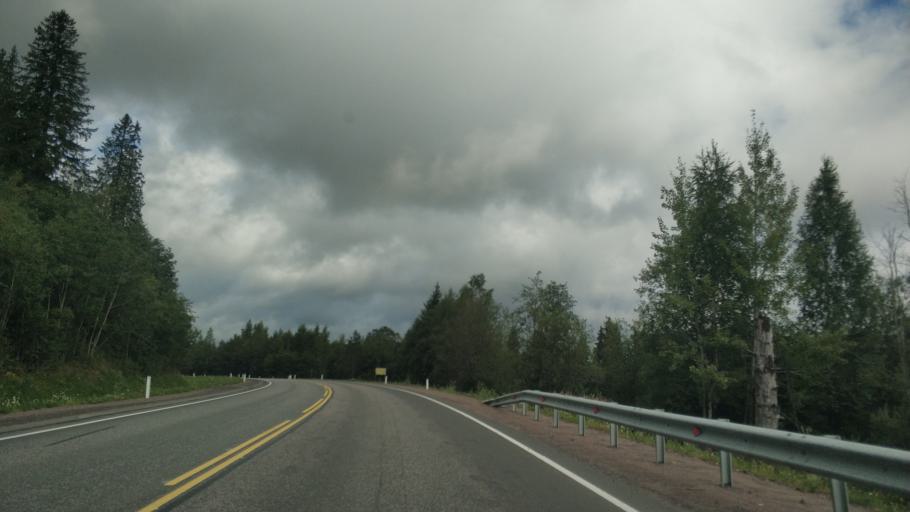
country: RU
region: Republic of Karelia
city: Khelyulya
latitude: 61.7840
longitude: 30.6547
